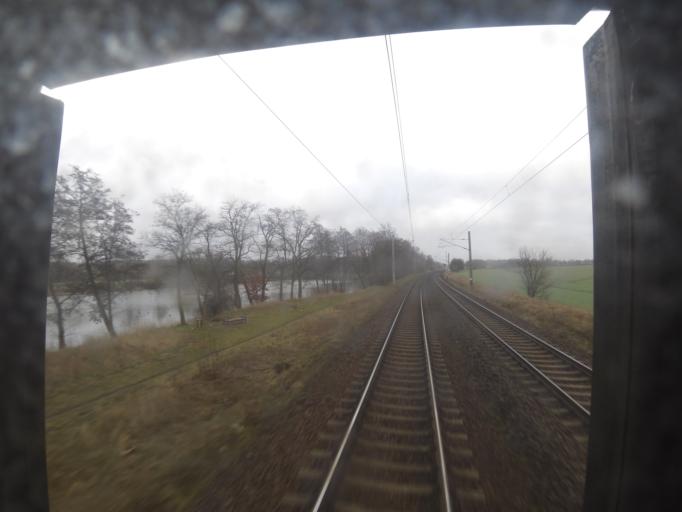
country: DE
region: Brandenburg
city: Rangsdorf
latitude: 52.2768
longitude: 13.4366
